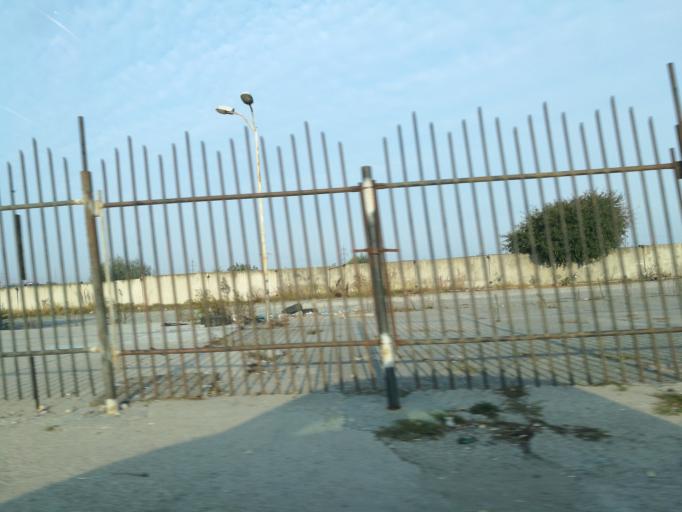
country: RO
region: Constanta
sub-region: Municipiul Constanta
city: Palazu Mare
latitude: 44.2027
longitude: 28.6096
